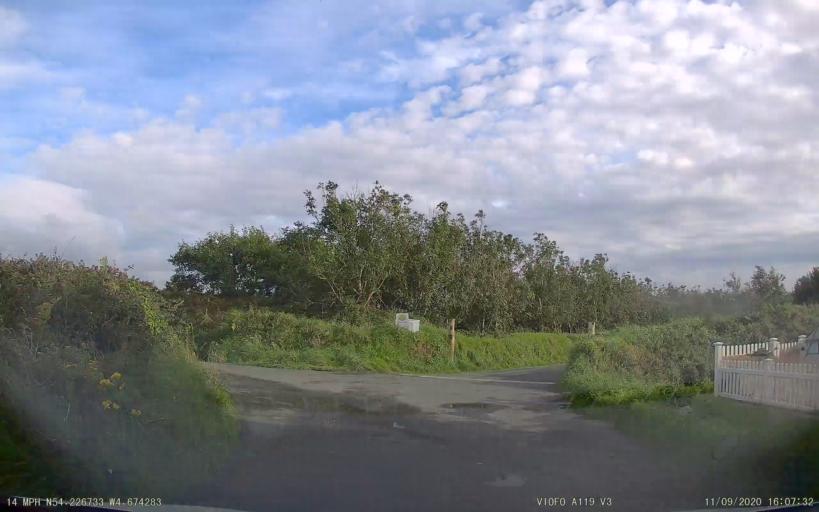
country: IM
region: Castletown
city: Castletown
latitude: 54.2268
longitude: -4.6743
